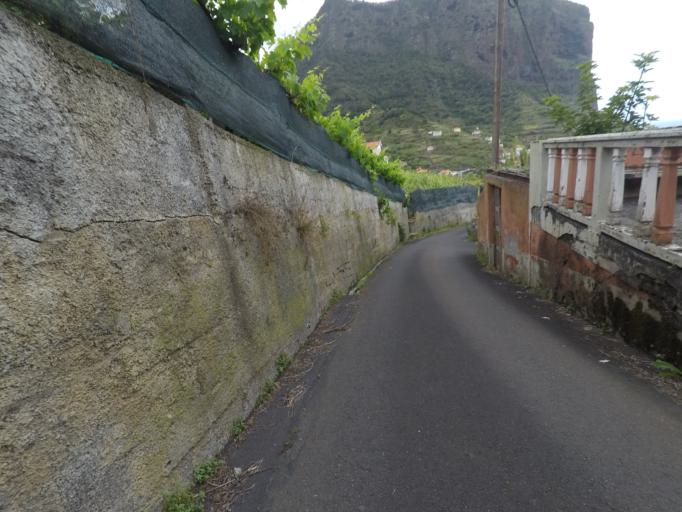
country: PT
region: Madeira
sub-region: Santana
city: Santana
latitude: 32.7689
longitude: -16.8311
